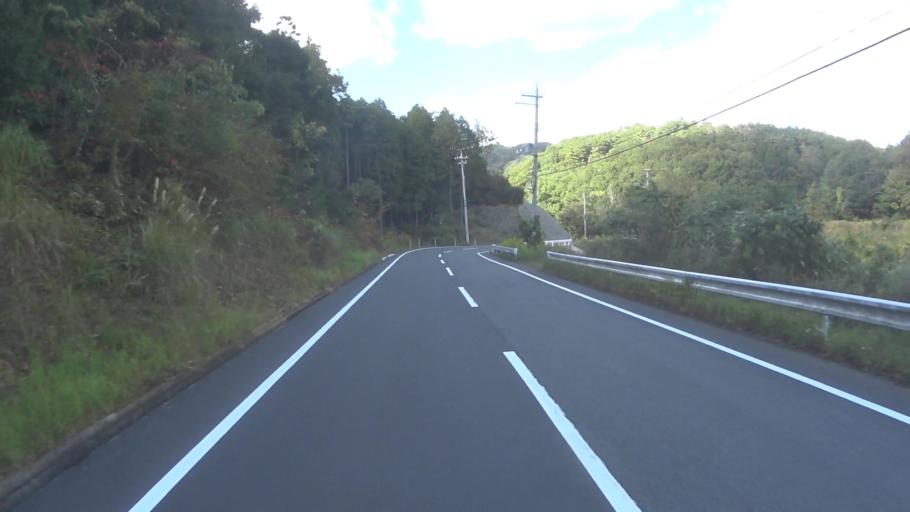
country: JP
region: Kyoto
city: Maizuru
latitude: 35.5508
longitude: 135.4475
